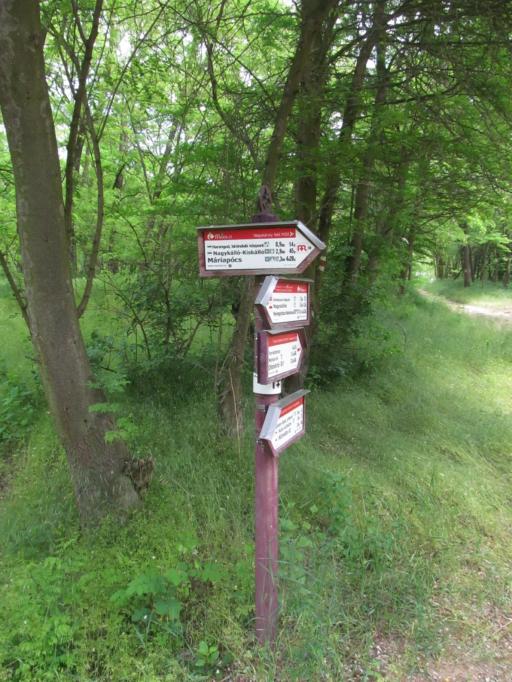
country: HU
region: Szabolcs-Szatmar-Bereg
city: Nagykallo
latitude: 47.9024
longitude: 21.8548
